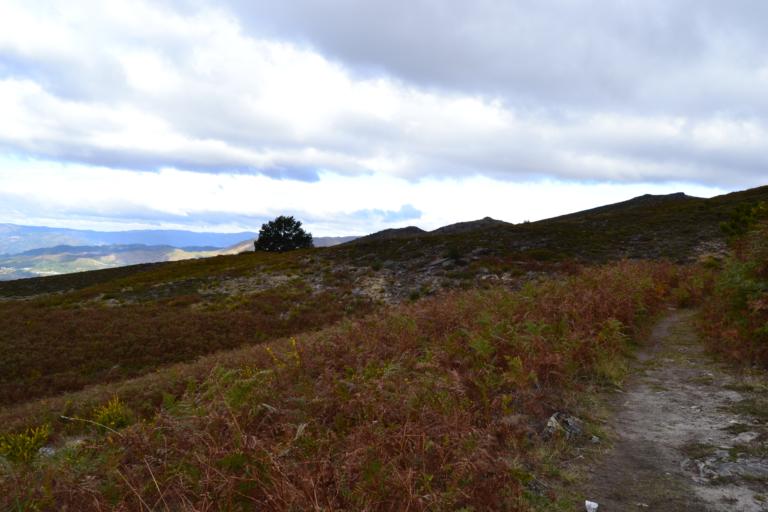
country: PT
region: Braga
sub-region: Terras de Bouro
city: Antas
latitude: 41.7881
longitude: -8.2640
